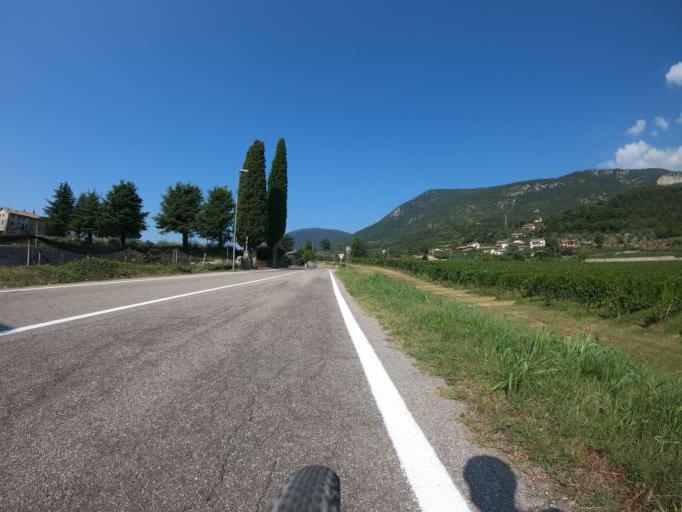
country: IT
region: Veneto
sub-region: Provincia di Verona
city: Caprino Veronese
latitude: 45.6091
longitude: 10.8135
